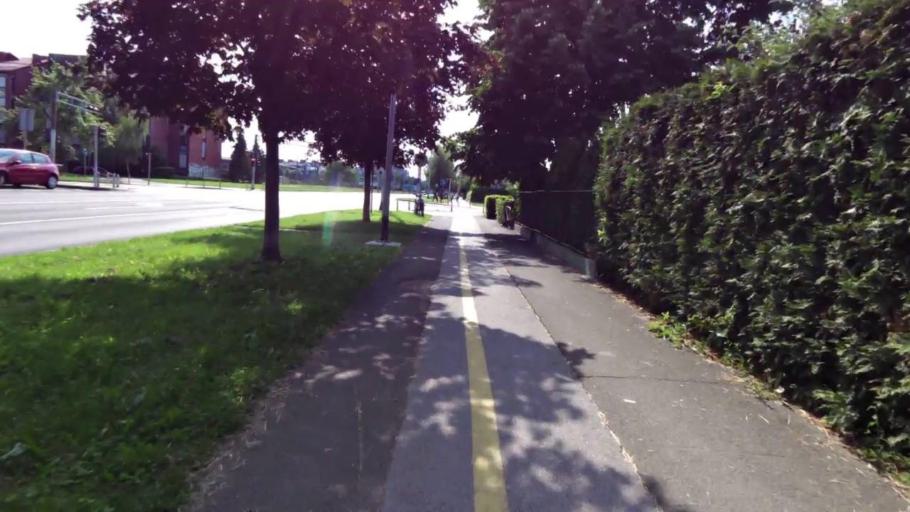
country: HR
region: Grad Zagreb
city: Jankomir
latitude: 45.8020
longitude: 15.9038
